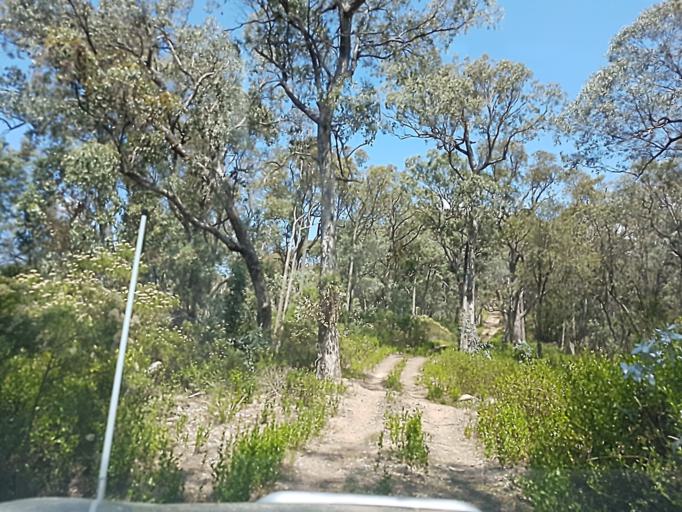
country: AU
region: Victoria
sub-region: East Gippsland
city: Lakes Entrance
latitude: -37.3099
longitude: 148.3587
